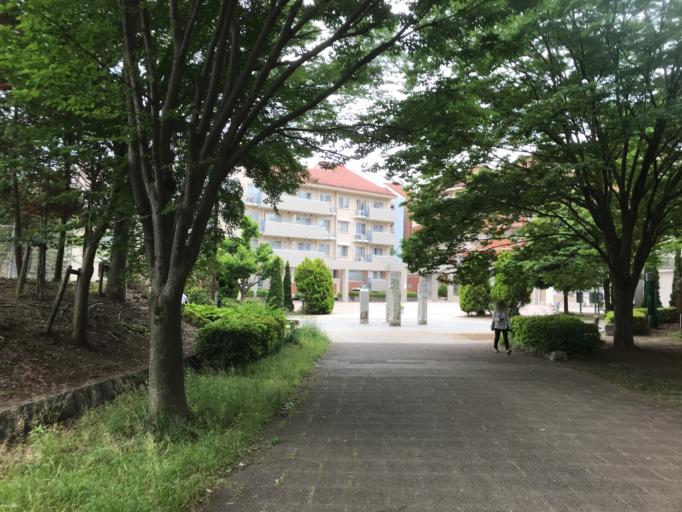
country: JP
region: Tokyo
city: Hachioji
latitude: 35.6123
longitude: 139.3724
